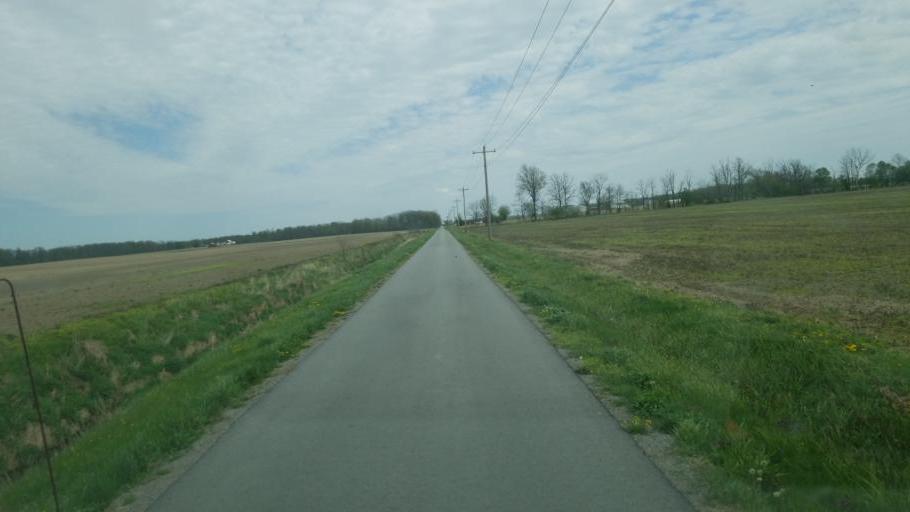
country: US
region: Ohio
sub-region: Hancock County
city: Arlington
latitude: 40.8483
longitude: -83.7457
